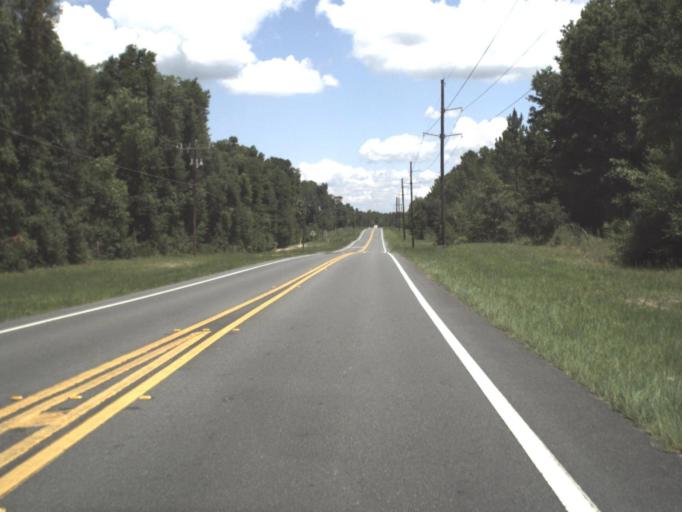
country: US
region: Florida
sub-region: Alachua County
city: Hawthorne
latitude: 29.6317
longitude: -82.0299
